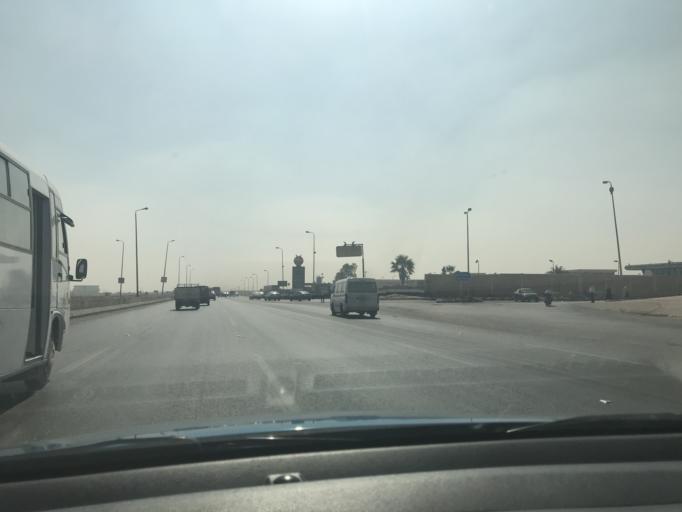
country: EG
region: Muhafazat al Qalyubiyah
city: Al Khankah
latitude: 30.1811
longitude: 31.6036
